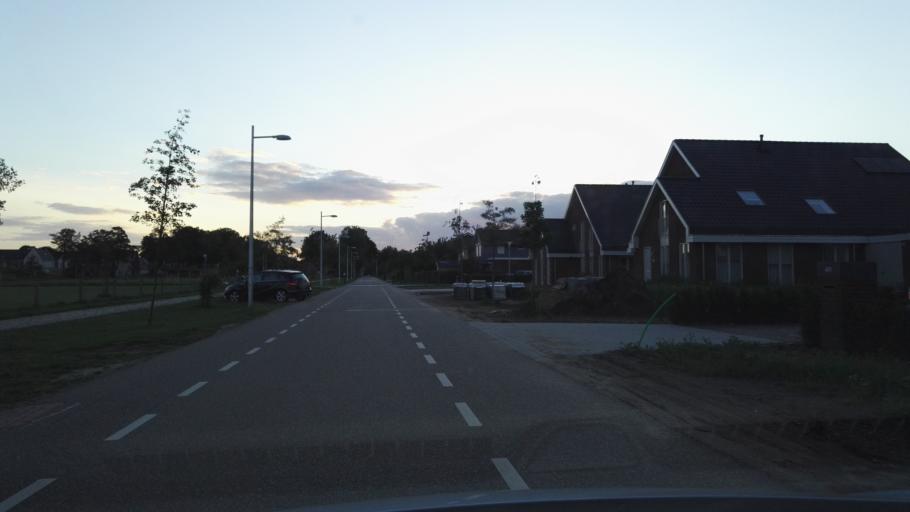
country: NL
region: Gelderland
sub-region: Gemeente Apeldoorn
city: Apeldoorn
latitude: 52.2051
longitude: 6.0111
